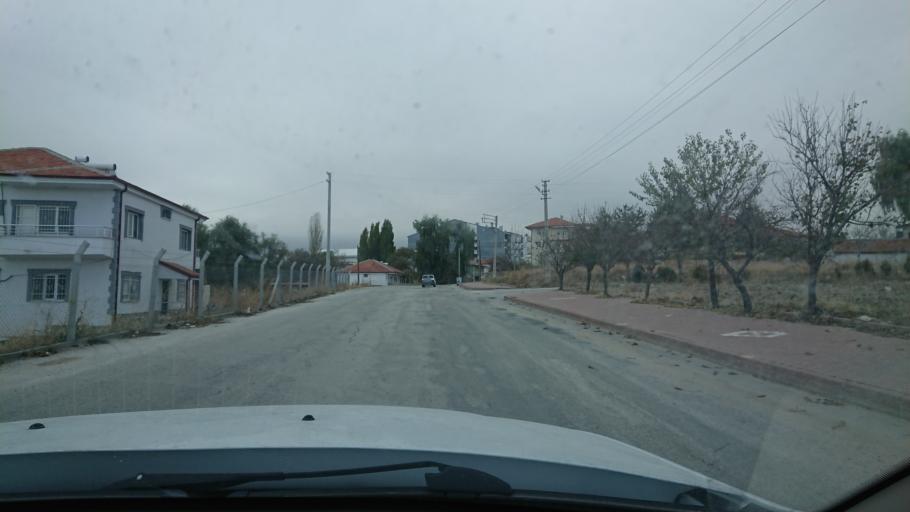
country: TR
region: Aksaray
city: Ortakoy
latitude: 38.7450
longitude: 34.0482
